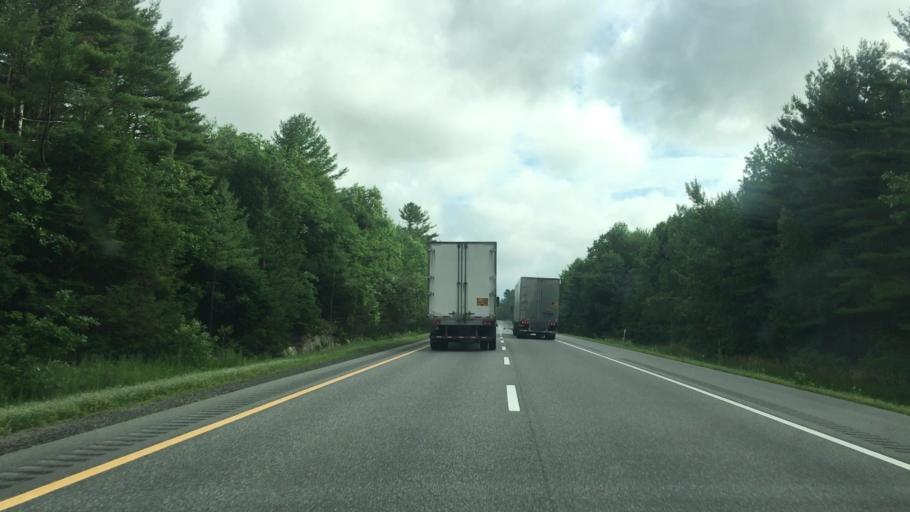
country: US
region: Maine
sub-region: Kennebec County
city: Sidney
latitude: 44.4284
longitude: -69.7366
